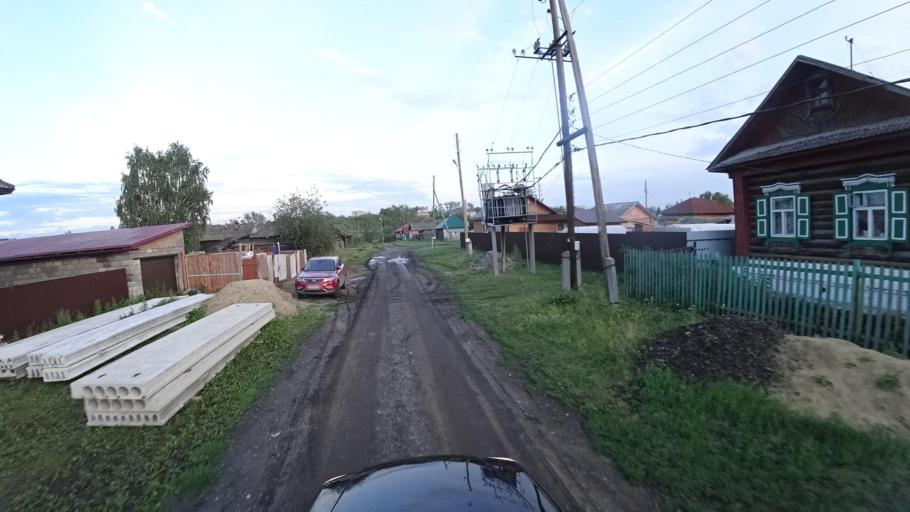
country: RU
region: Sverdlovsk
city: Kamyshlov
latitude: 56.8587
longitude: 62.7140
